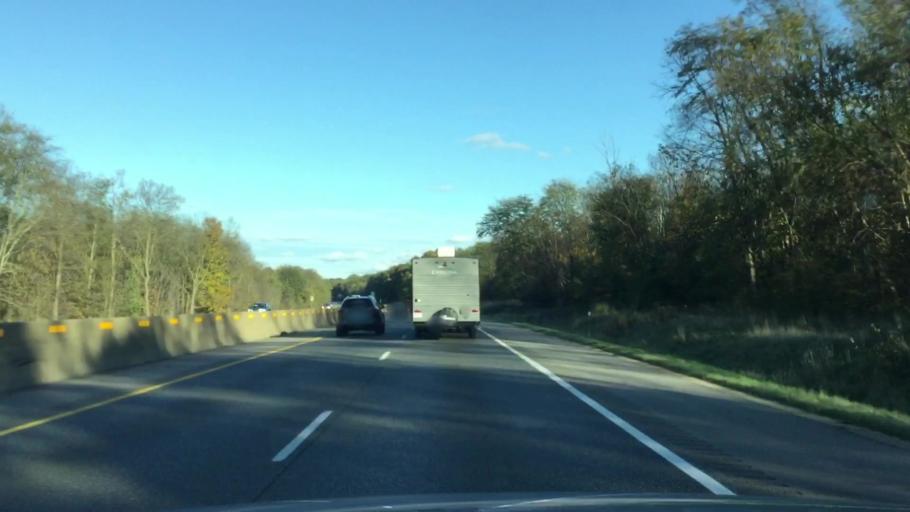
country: US
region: Michigan
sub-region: Kalamazoo County
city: Galesburg
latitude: 42.2693
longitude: -85.4589
